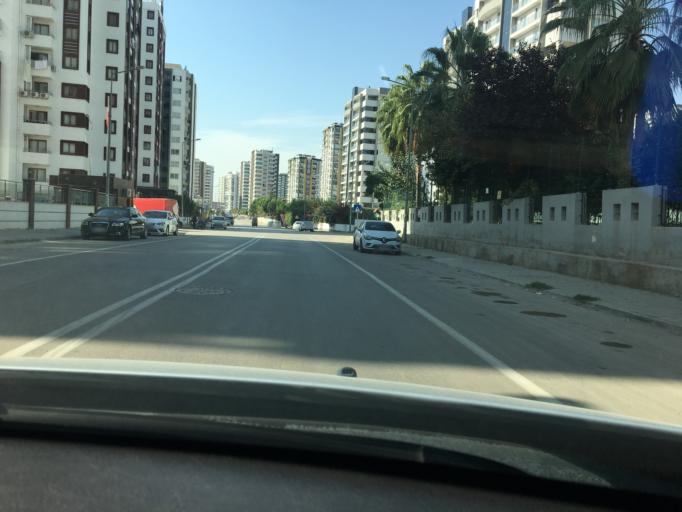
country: TR
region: Adana
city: Seyhan
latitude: 37.0194
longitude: 35.2629
